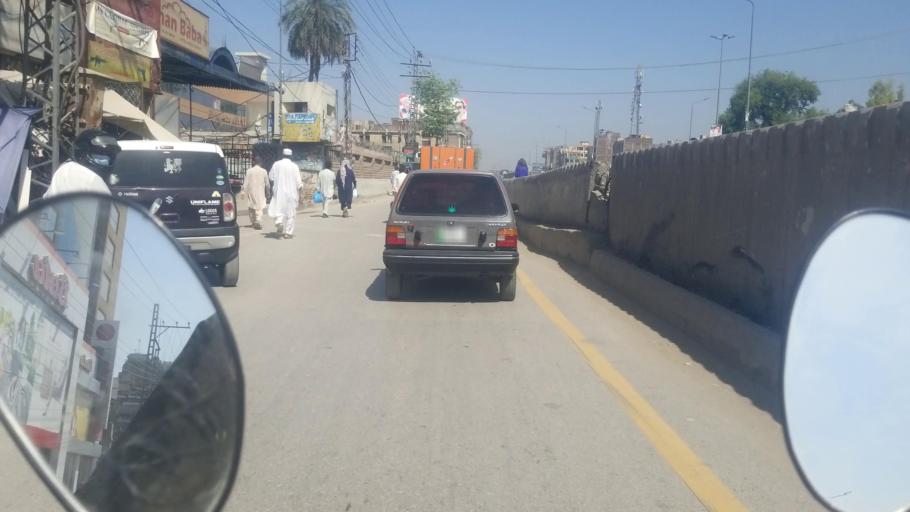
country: PK
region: Khyber Pakhtunkhwa
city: Peshawar
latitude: 34.0150
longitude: 71.5766
